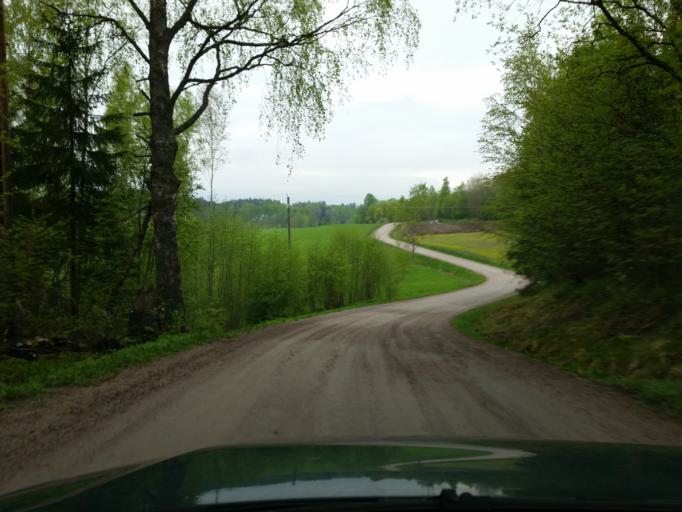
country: FI
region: Uusimaa
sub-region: Helsinki
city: Karjalohja
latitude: 60.1834
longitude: 23.6834
